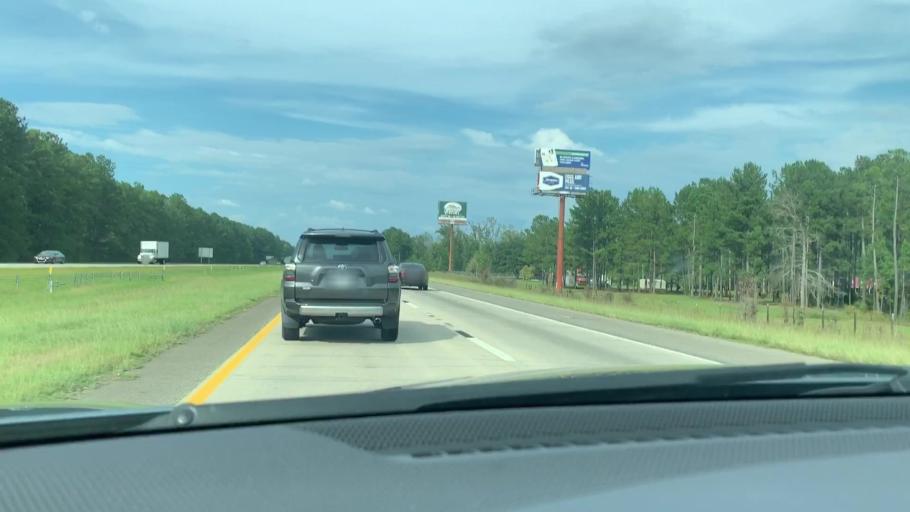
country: US
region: South Carolina
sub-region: Colleton County
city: Walterboro
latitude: 32.9439
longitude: -80.6841
